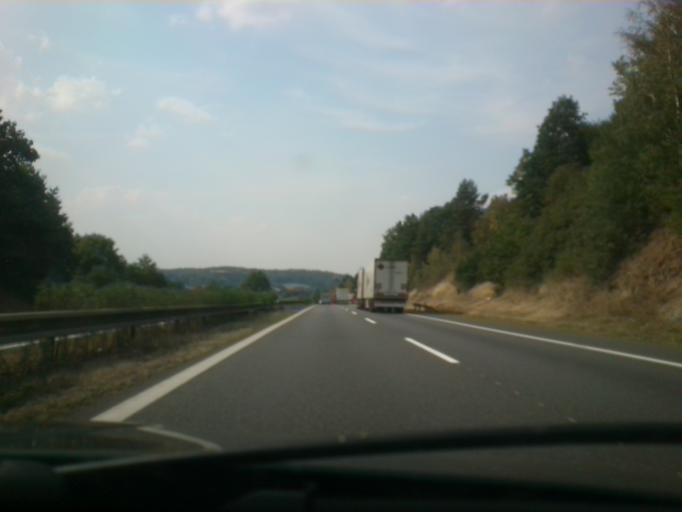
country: CZ
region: Central Bohemia
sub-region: Okres Praha-Vychod
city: Mnichovice
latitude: 49.9038
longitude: 14.7363
